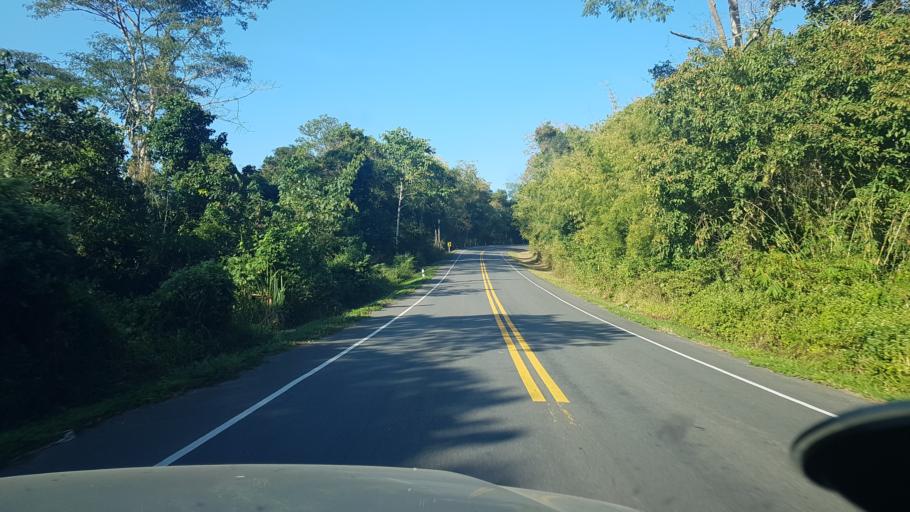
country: TH
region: Phetchabun
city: Nam Nao
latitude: 16.7610
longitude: 101.4773
